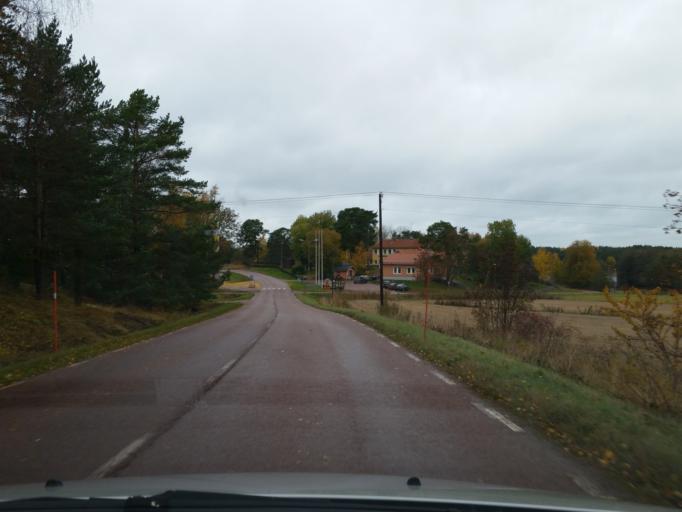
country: AX
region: Alands landsbygd
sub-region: Lumparland
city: Lumparland
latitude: 60.1160
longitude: 20.2609
